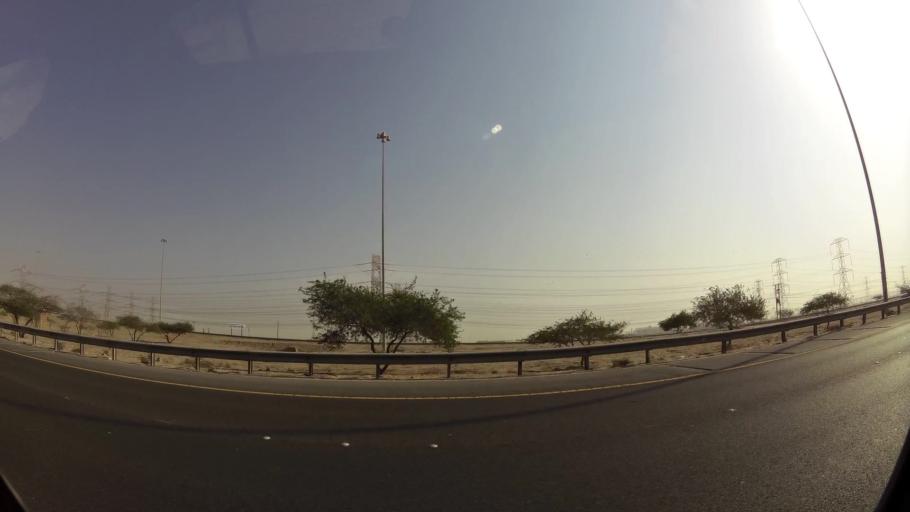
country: KW
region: Al Ahmadi
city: Al Ahmadi
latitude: 28.9891
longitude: 48.1031
